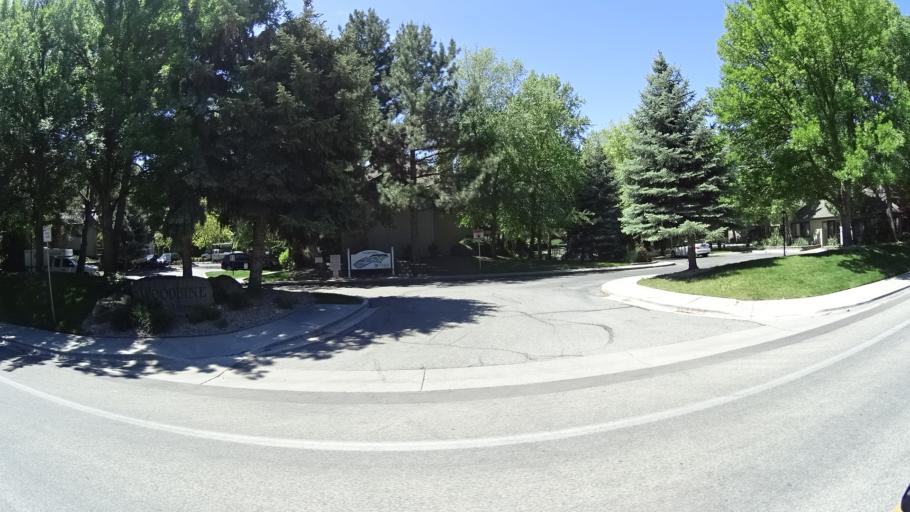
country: US
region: Idaho
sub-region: Ada County
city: Boise
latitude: 43.5697
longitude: -116.1822
